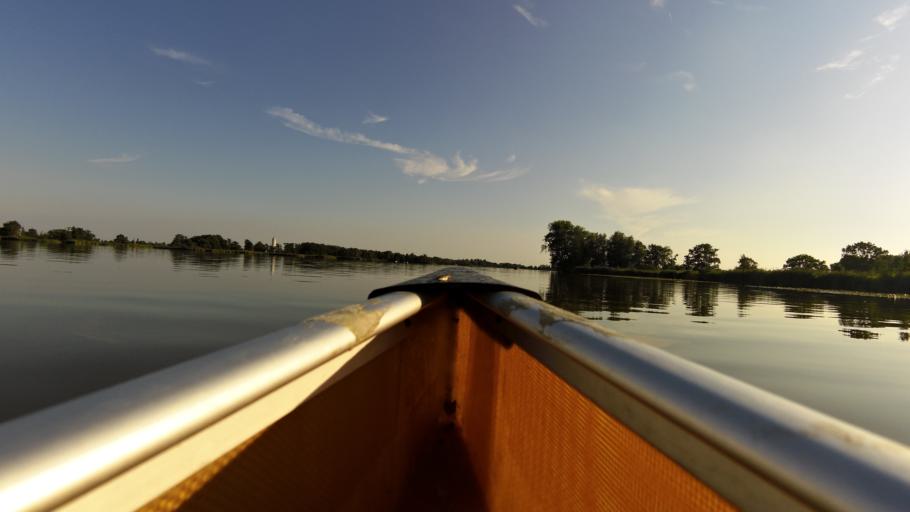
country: NL
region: South Holland
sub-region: Gemeente Nieuwkoop
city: Nieuwkoop
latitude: 52.1327
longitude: 4.7798
